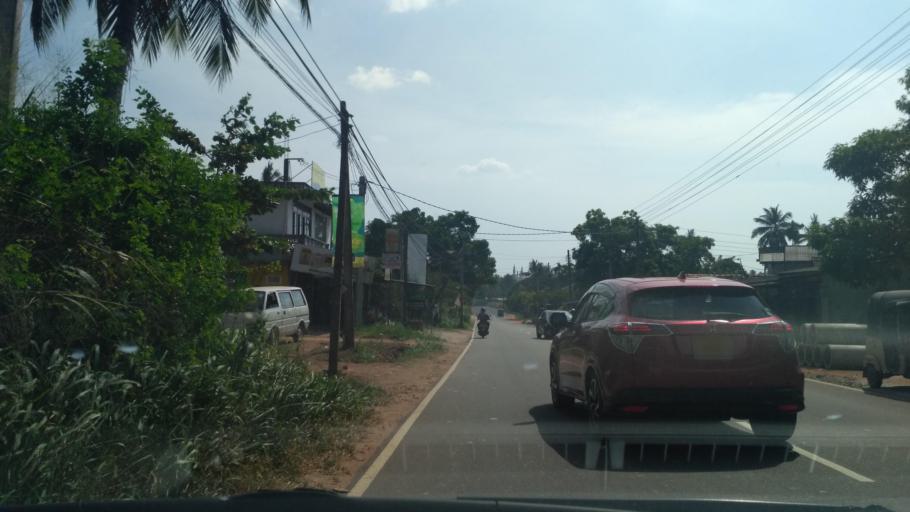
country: LK
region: North Western
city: Kuliyapitiya
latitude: 7.3587
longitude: 80.0328
